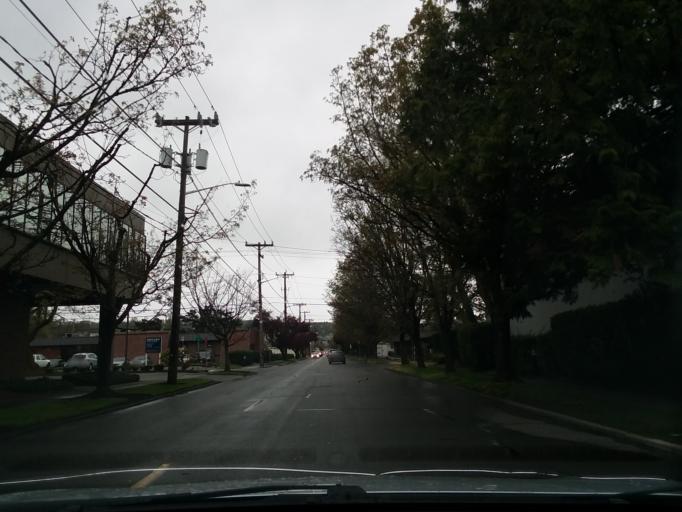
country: US
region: Washington
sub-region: King County
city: White Center
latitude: 47.5534
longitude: -122.3262
